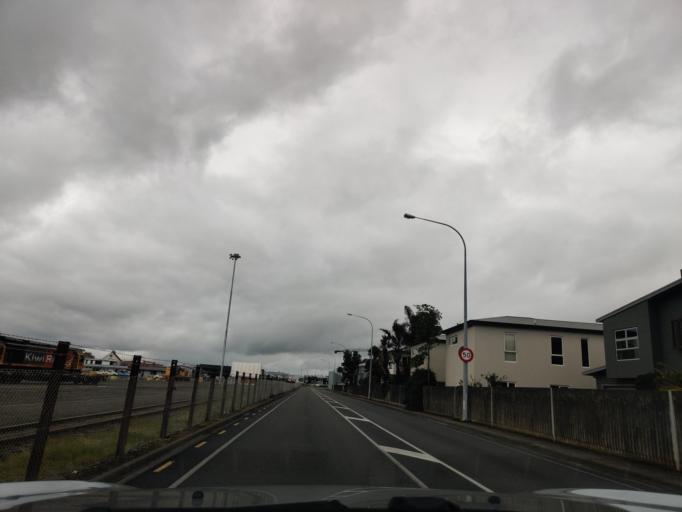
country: NZ
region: Hawke's Bay
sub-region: Napier City
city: Napier
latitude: -39.4805
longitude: 176.9009
